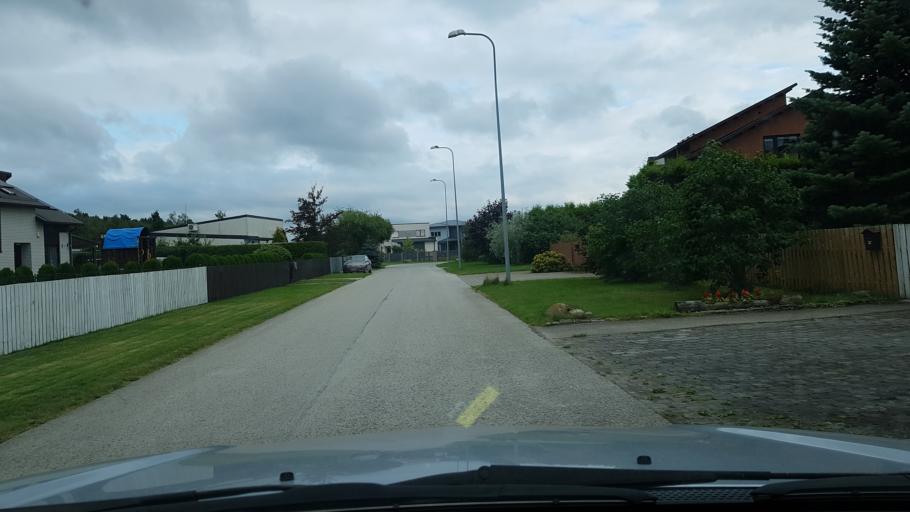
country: EE
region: Harju
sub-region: Tallinna linn
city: Tallinn
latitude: 59.4034
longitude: 24.8207
